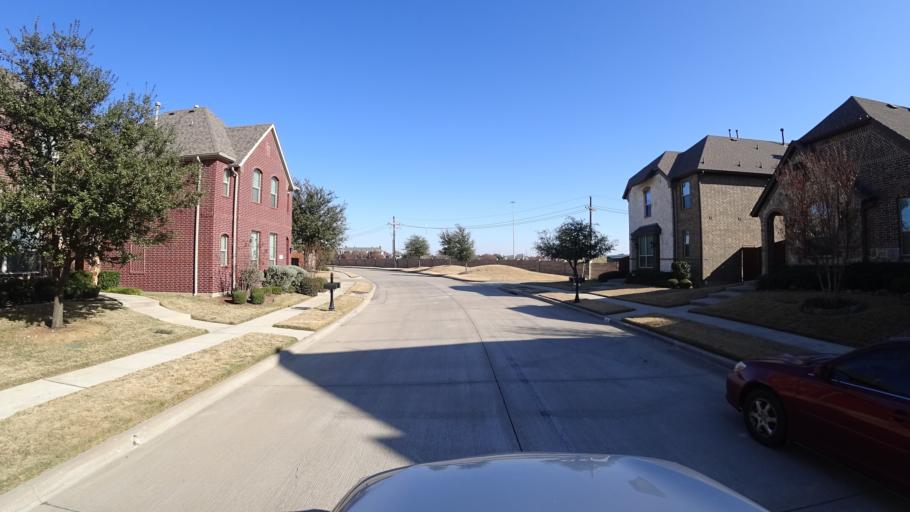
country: US
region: Texas
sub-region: Denton County
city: Lewisville
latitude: 33.0048
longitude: -96.9956
